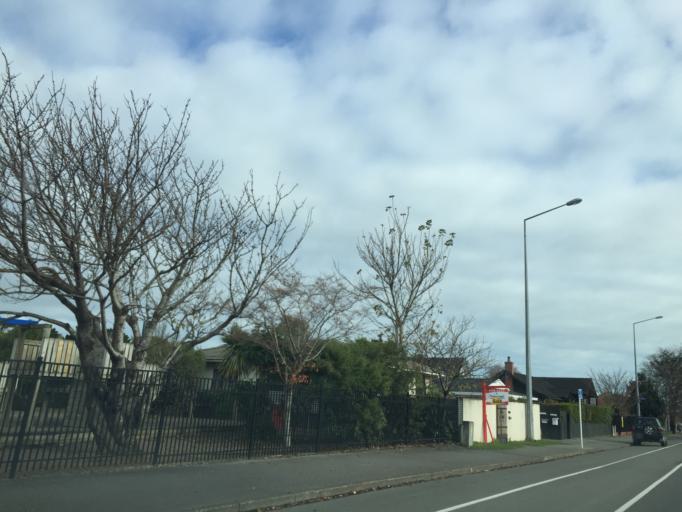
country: NZ
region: Southland
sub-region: Invercargill City
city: Invercargill
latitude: -46.3948
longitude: 168.3537
